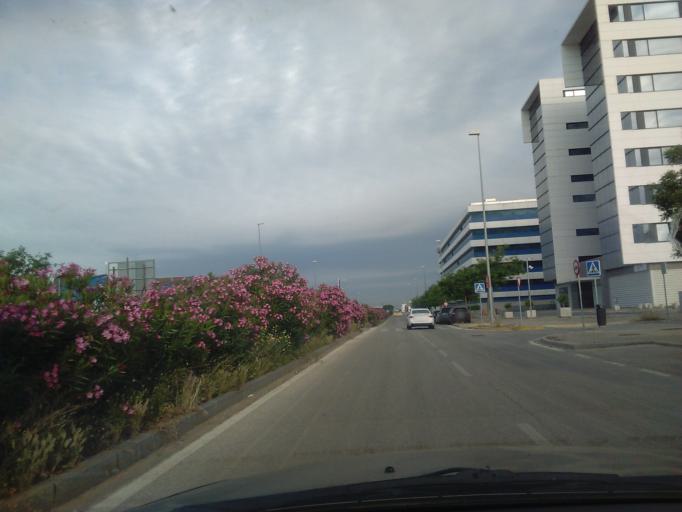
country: ES
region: Andalusia
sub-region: Provincia de Sevilla
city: Sevilla
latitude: 37.3818
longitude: -5.9166
